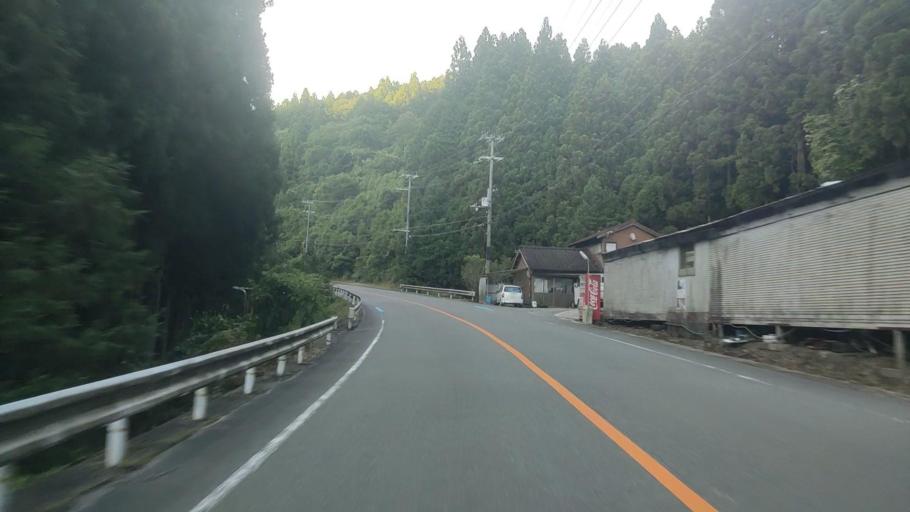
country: JP
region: Wakayama
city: Tanabe
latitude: 33.8133
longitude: 135.6158
